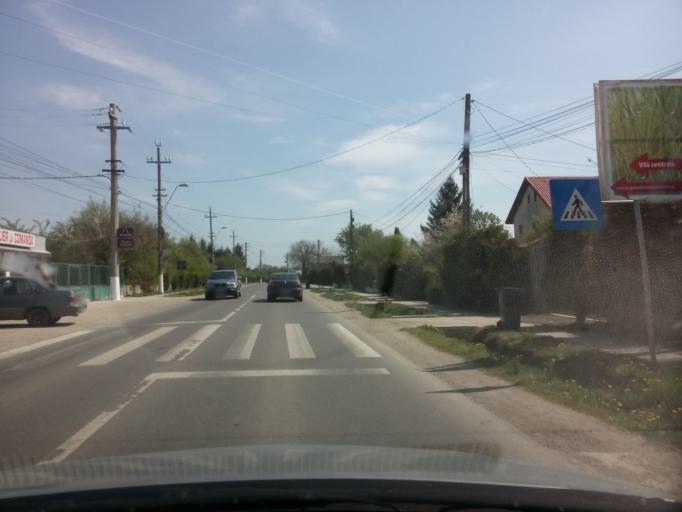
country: RO
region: Ilfov
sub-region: Comuna Corbeanca
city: Corbeanca
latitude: 44.5933
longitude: 26.0340
